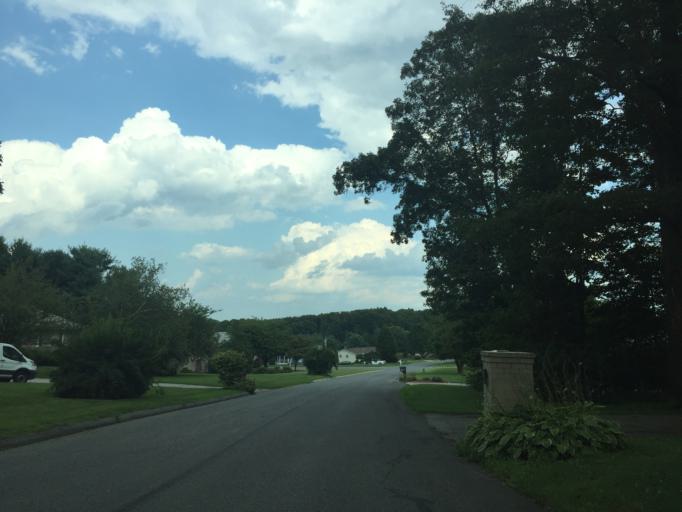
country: US
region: Maryland
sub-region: Carroll County
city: Manchester
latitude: 39.6215
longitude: -76.9161
